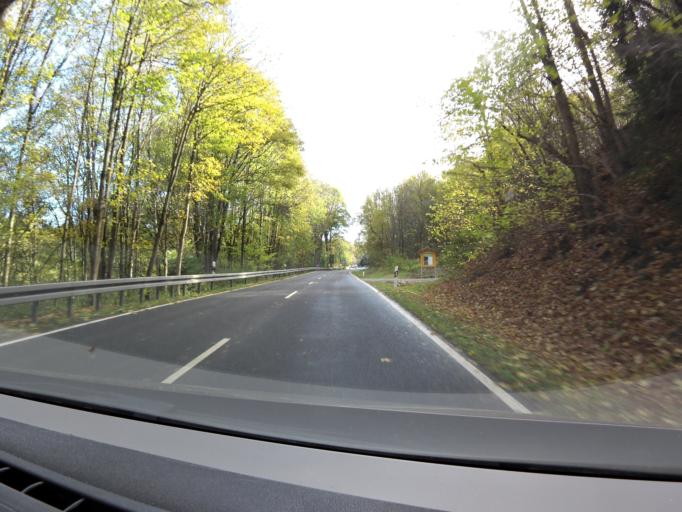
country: DE
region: Thuringia
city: Martinroda
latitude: 50.6999
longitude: 10.8861
